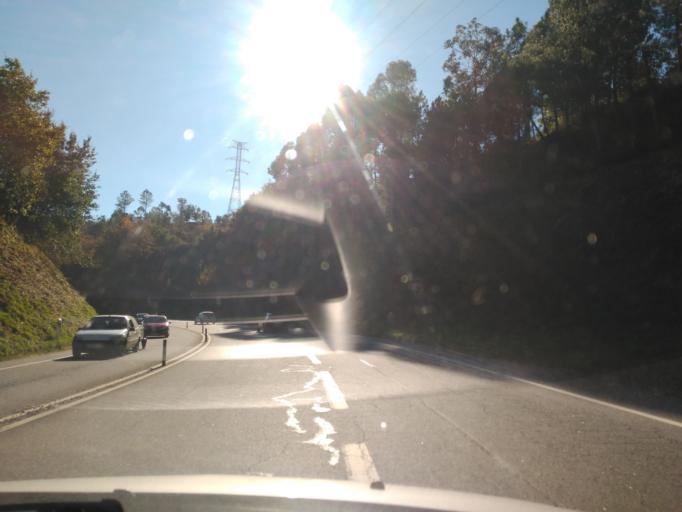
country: PT
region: Braga
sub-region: Amares
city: Amares
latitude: 41.5895
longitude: -8.3424
